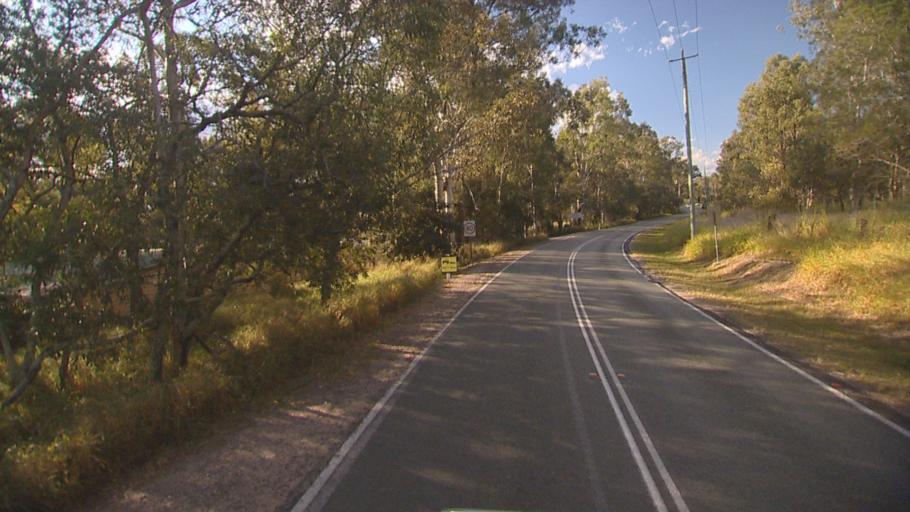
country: AU
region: Queensland
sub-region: Ipswich
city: Springfield Lakes
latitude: -27.7322
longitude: 152.9471
